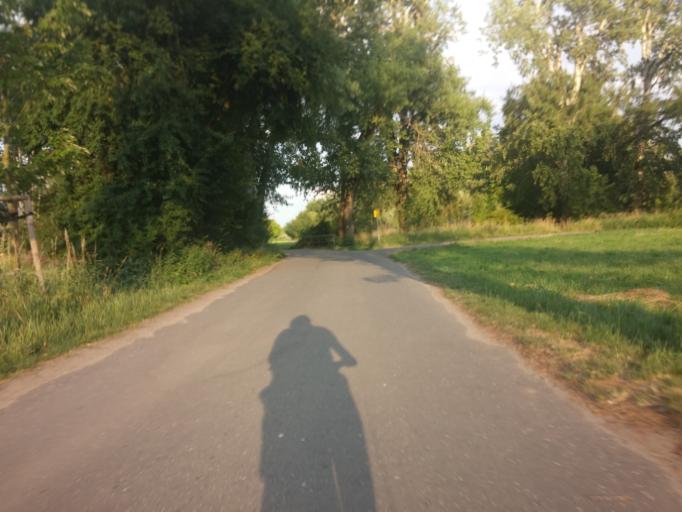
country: CZ
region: Central Bohemia
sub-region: Okres Nymburk
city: Podebrady
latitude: 50.1388
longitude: 15.1169
